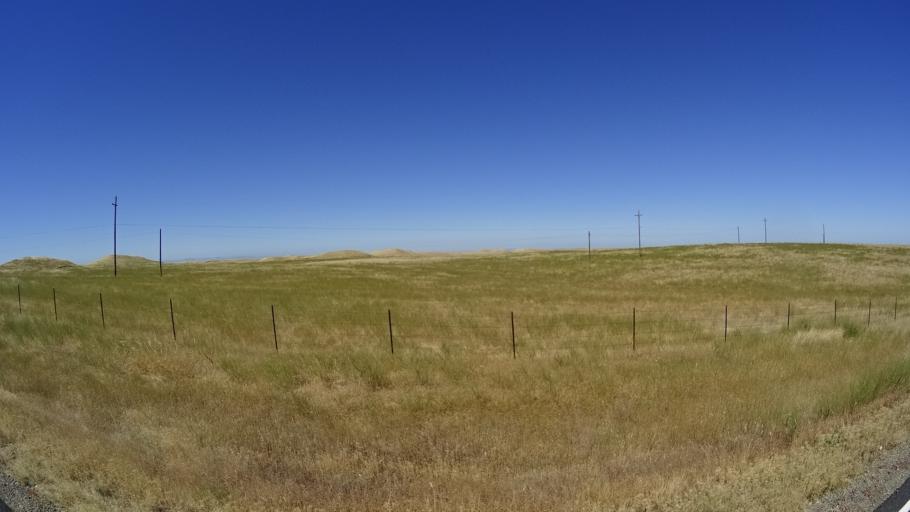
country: US
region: California
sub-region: Calaveras County
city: Rancho Calaveras
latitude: 38.0388
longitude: -120.8560
